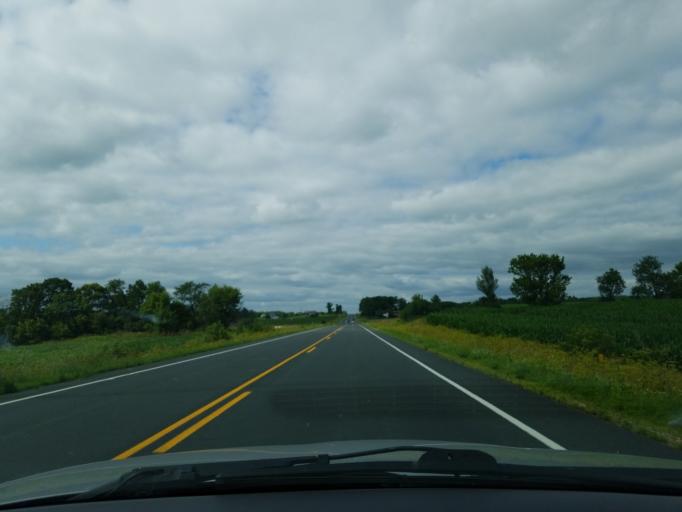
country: US
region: Wisconsin
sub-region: Saint Croix County
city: Hammond
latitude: 45.0275
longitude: -92.4364
